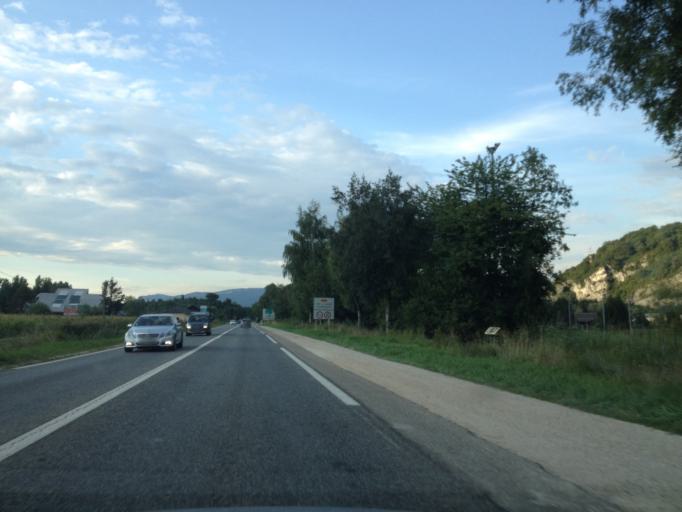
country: FR
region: Rhone-Alpes
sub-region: Departement de la Savoie
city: Voglans
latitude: 45.6332
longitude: 5.8920
